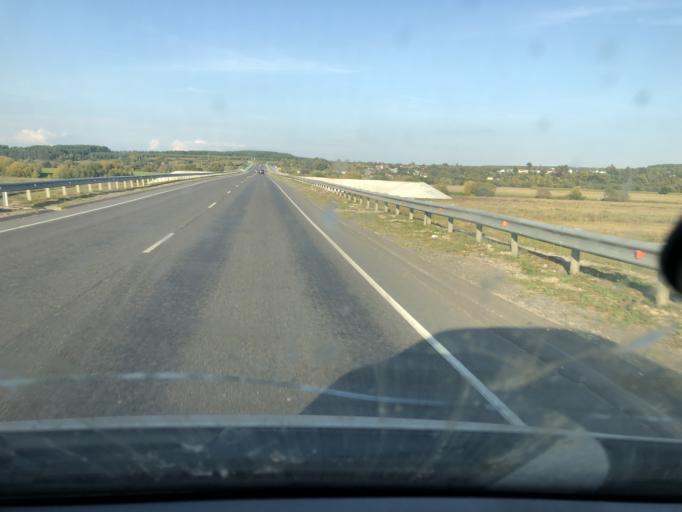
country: RU
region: Kaluga
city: Peremyshl'
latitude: 54.2878
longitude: 36.1652
